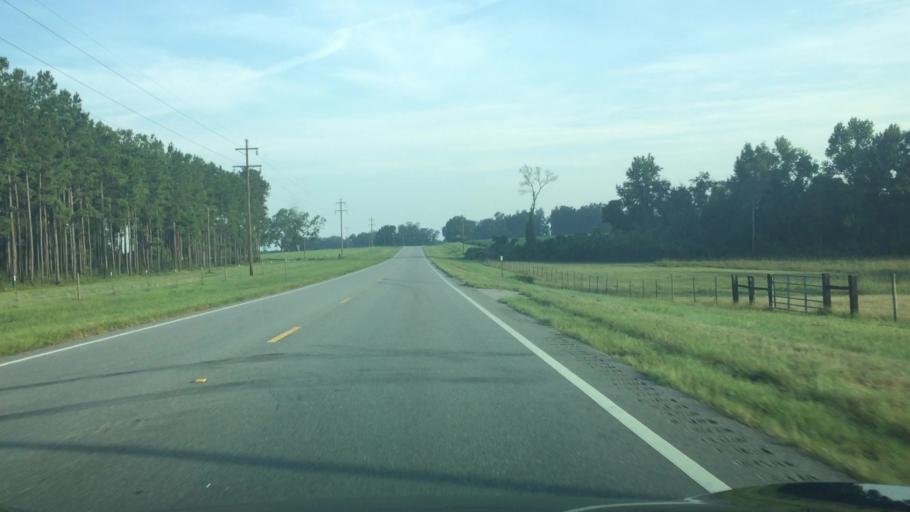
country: US
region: Alabama
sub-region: Covington County
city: Florala
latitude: 31.0439
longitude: -86.3829
